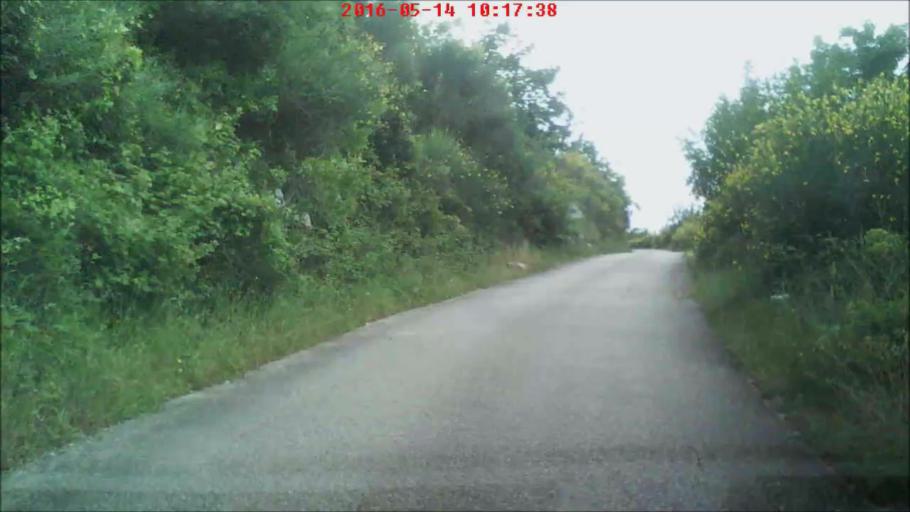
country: HR
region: Dubrovacko-Neretvanska
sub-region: Grad Dubrovnik
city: Mokosica
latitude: 42.7225
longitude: 17.9690
